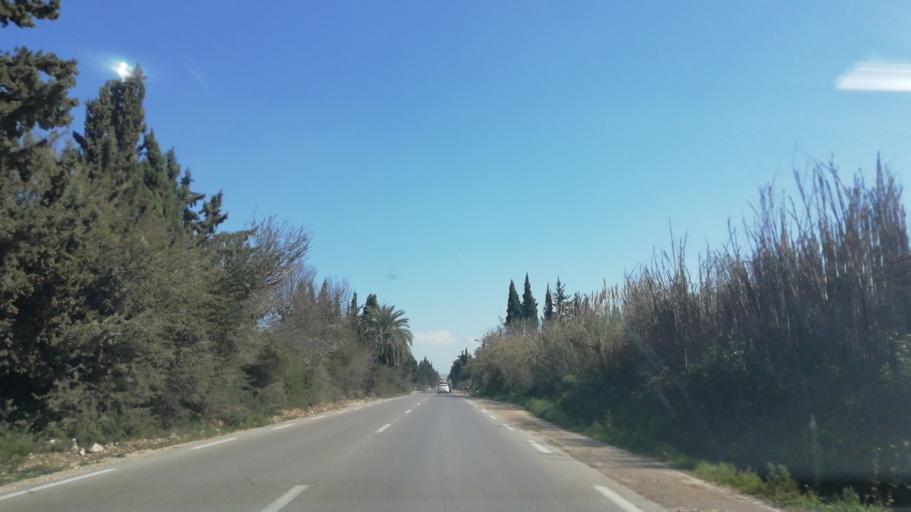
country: DZ
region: Mascara
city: Mascara
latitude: 35.5809
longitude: 0.0218
